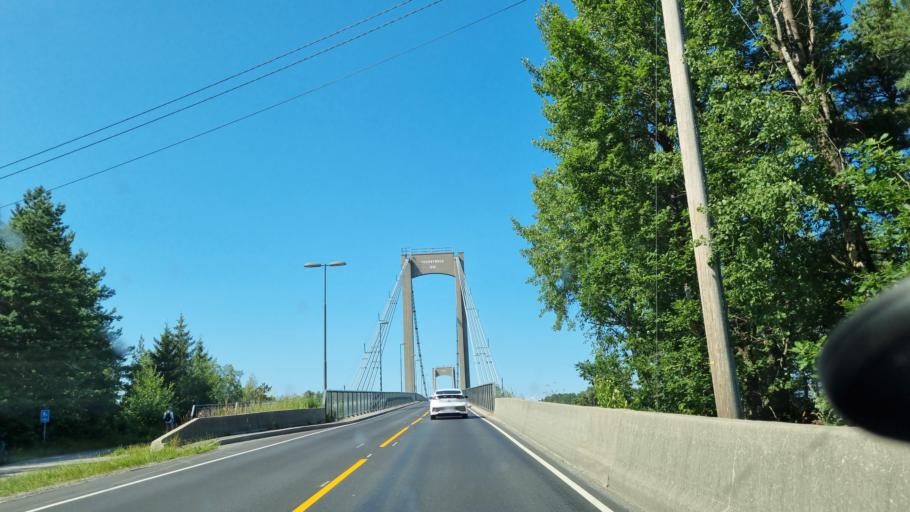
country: NO
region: Aust-Agder
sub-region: Arendal
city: Arendal
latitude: 58.4689
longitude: 8.8241
